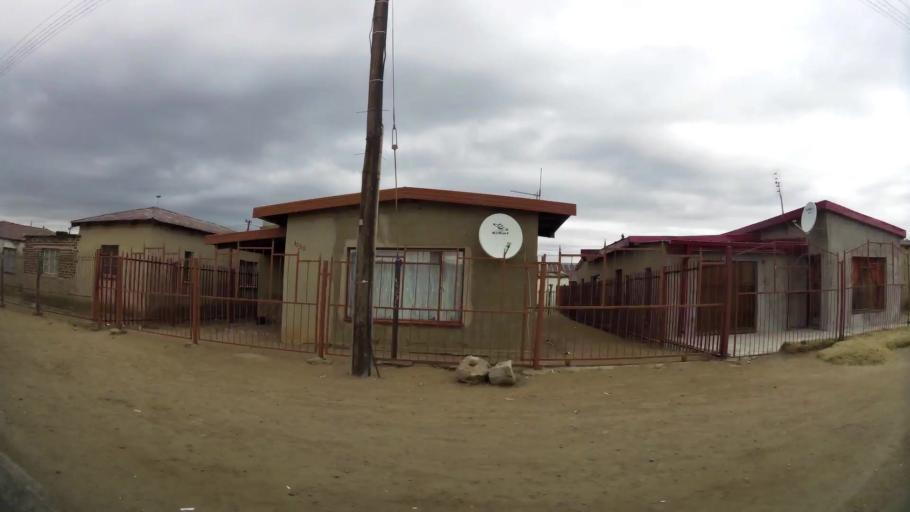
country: ZA
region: Orange Free State
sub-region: Fezile Dabi District Municipality
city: Kroonstad
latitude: -27.6512
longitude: 27.2002
